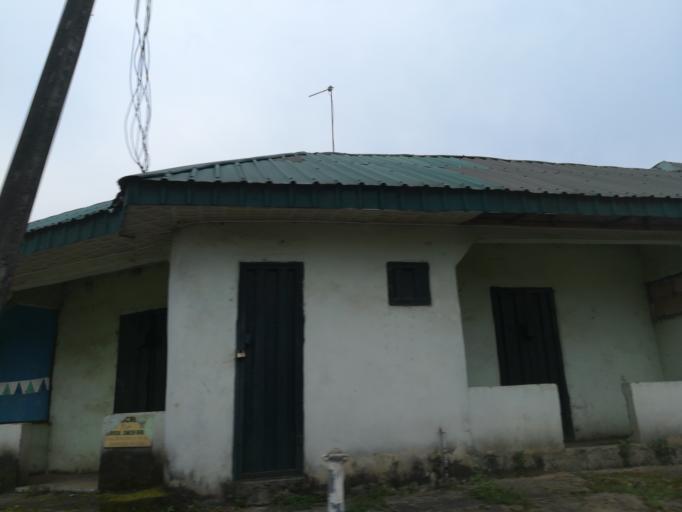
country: NG
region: Rivers
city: Okrika
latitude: 4.7812
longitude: 7.1292
